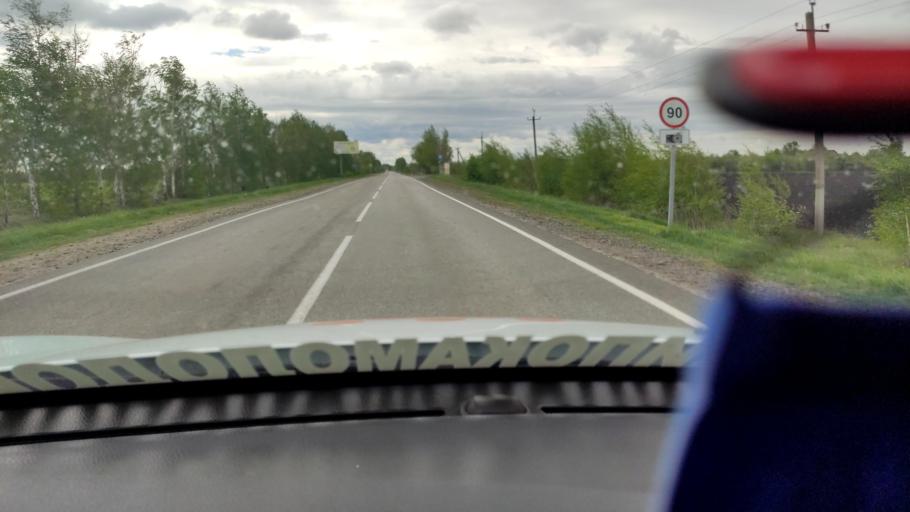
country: RU
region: Voronezj
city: Imeni Pervogo Maya
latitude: 50.7730
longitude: 39.3857
